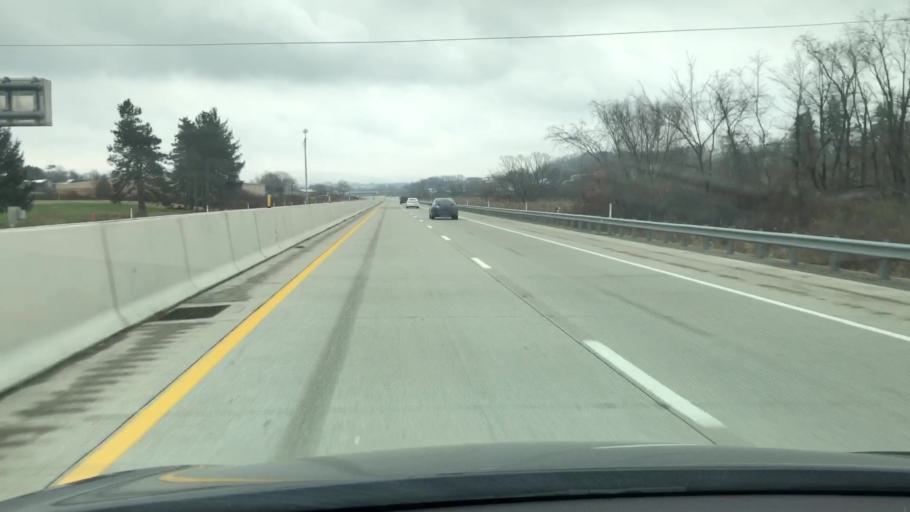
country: US
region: Pennsylvania
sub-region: Westmoreland County
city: Mount Pleasant
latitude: 40.1343
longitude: -79.5581
